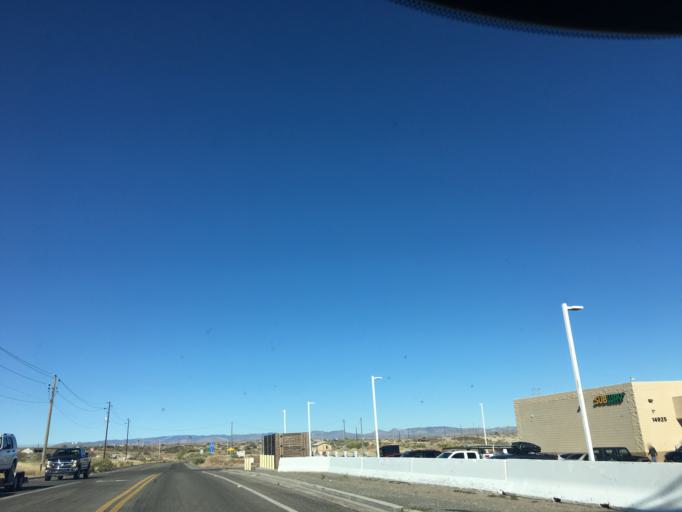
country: US
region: Arizona
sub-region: Yavapai County
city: Cordes Lakes
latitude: 34.3269
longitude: -112.1184
